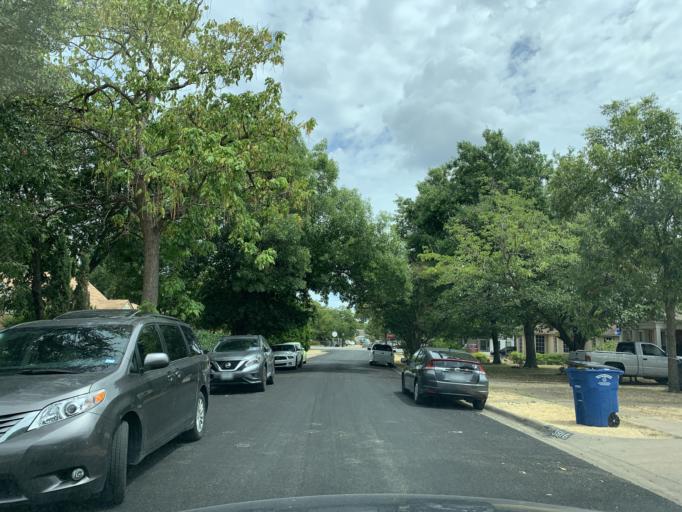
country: US
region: Texas
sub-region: Dallas County
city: Cockrell Hill
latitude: 32.7434
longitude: -96.8816
